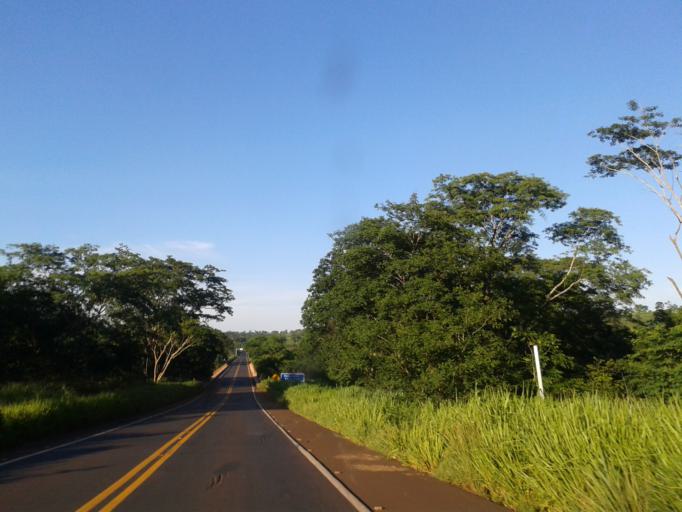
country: BR
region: Minas Gerais
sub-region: Ituiutaba
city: Ituiutaba
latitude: -18.9345
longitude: -49.7974
